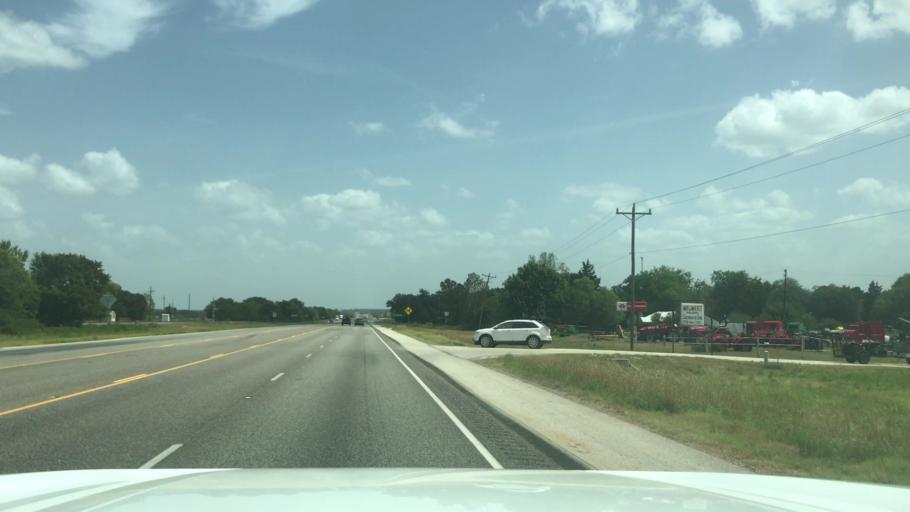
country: US
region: Texas
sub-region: Robertson County
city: Calvert
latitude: 30.9641
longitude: -96.6618
